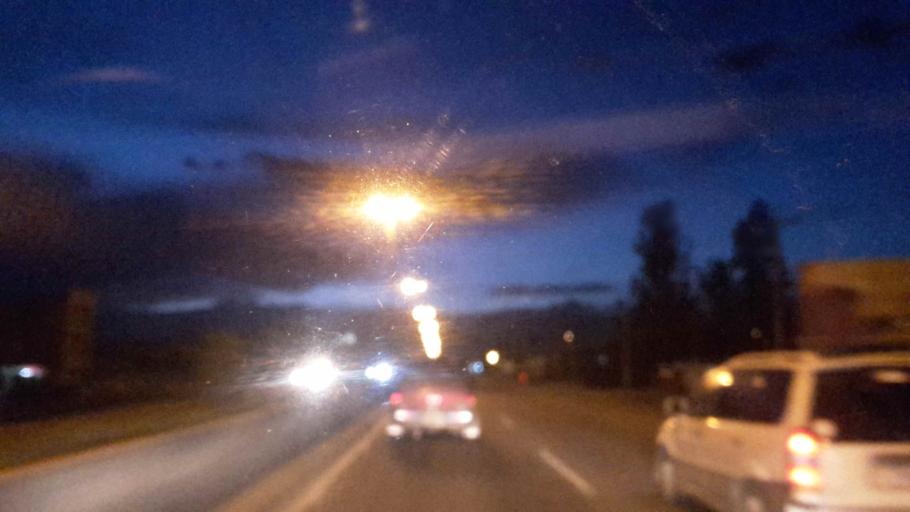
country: BO
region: Cochabamba
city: Cochabamba
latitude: -17.3907
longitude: -66.0775
